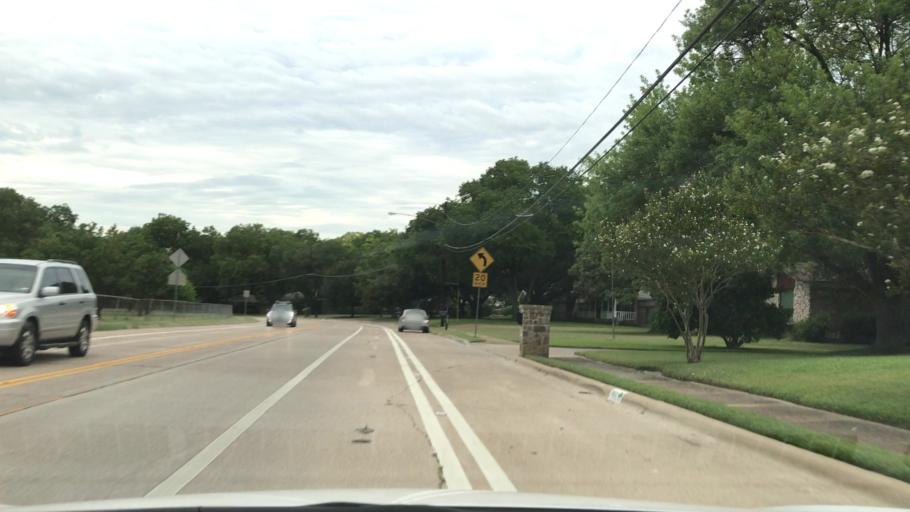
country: US
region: Texas
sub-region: Dallas County
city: Addison
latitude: 32.9323
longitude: -96.7826
